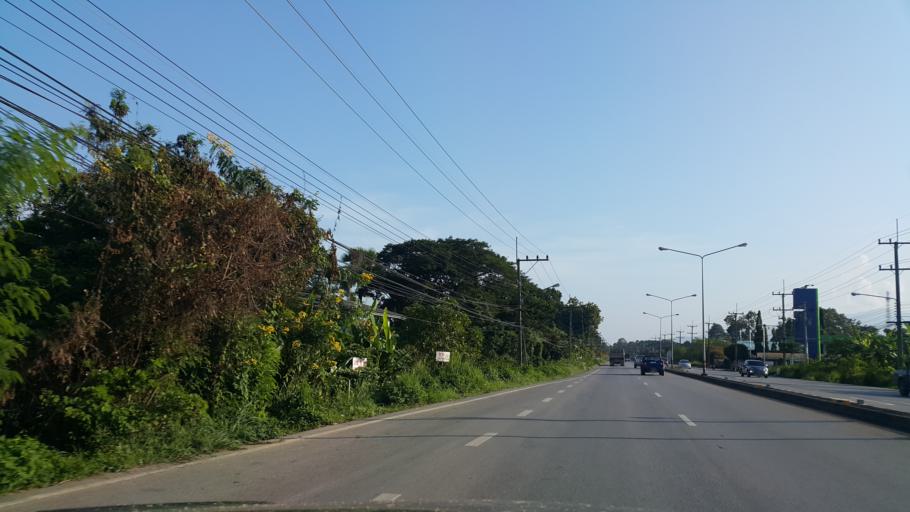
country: TH
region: Chiang Mai
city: Mae Taeng
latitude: 19.0089
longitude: 98.9446
